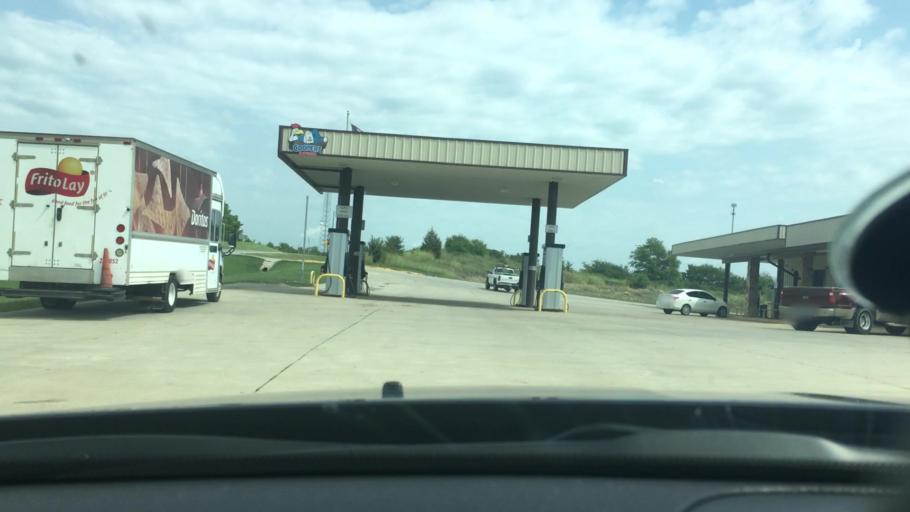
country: US
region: Oklahoma
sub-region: Coal County
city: Coalgate
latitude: 34.6078
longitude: -96.4241
